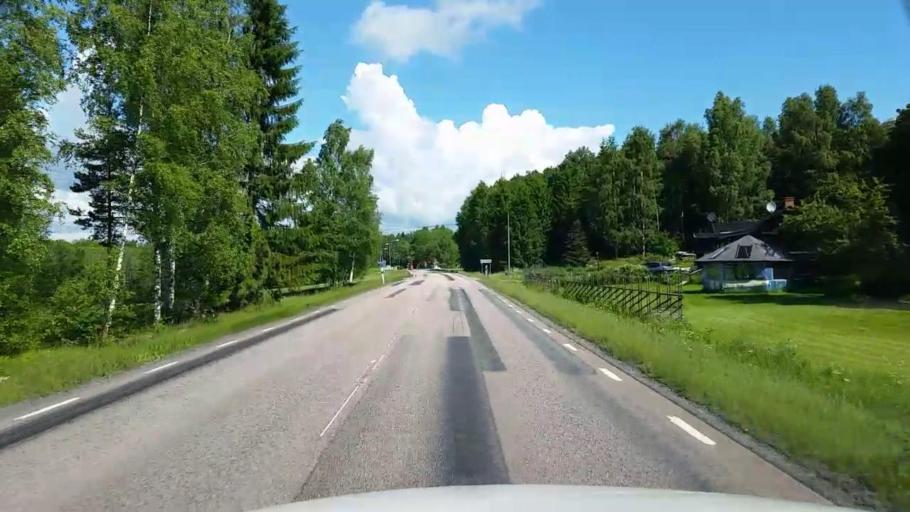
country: SE
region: Vaestmanland
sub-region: Kopings Kommun
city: Kolsva
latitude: 59.6212
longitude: 15.8205
